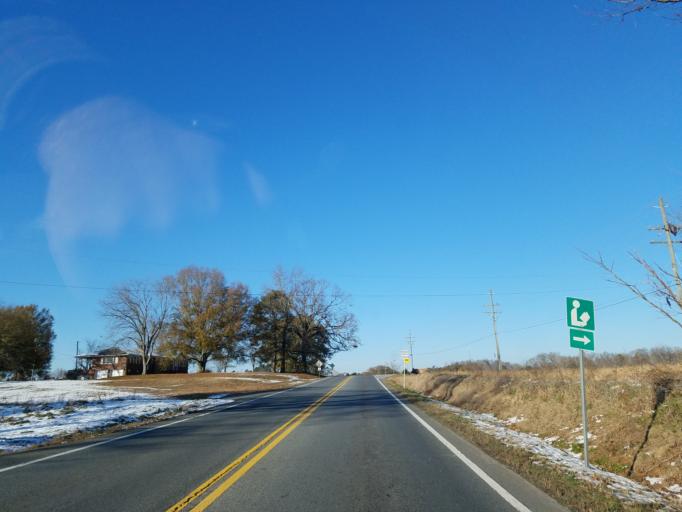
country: US
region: Georgia
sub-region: Dawson County
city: Dawsonville
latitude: 34.3549
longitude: -84.0321
